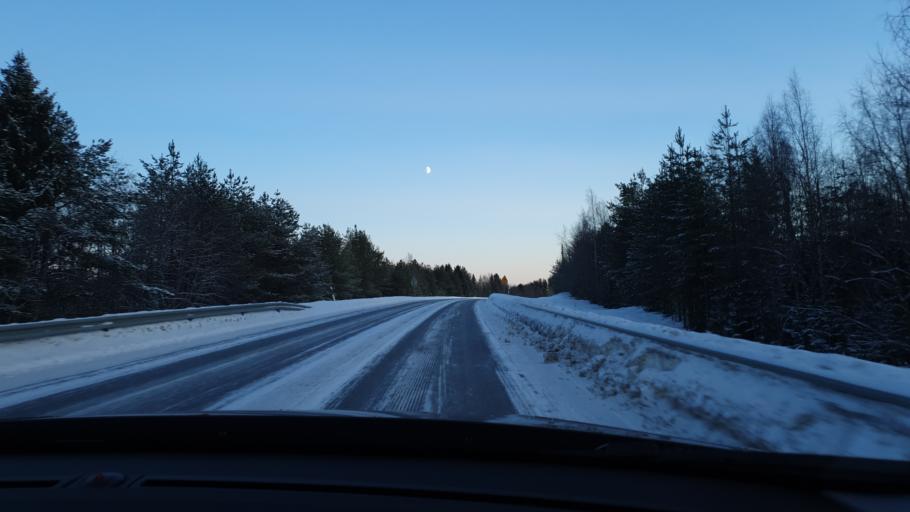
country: FI
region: Kainuu
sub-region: Kajaani
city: Sotkamo
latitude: 64.0989
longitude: 28.5290
